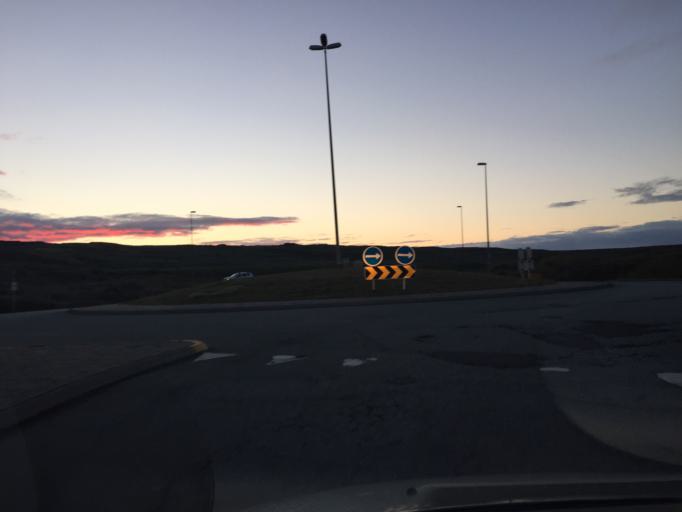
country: IS
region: Southern Peninsula
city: Vogar
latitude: 63.9630
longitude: -22.4206
